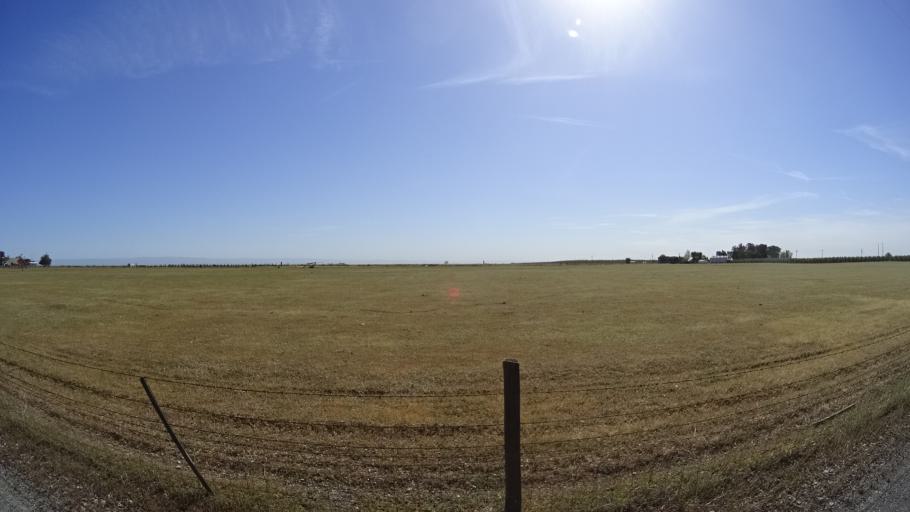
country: US
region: California
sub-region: Glenn County
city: Willows
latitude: 39.6135
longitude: -122.1564
